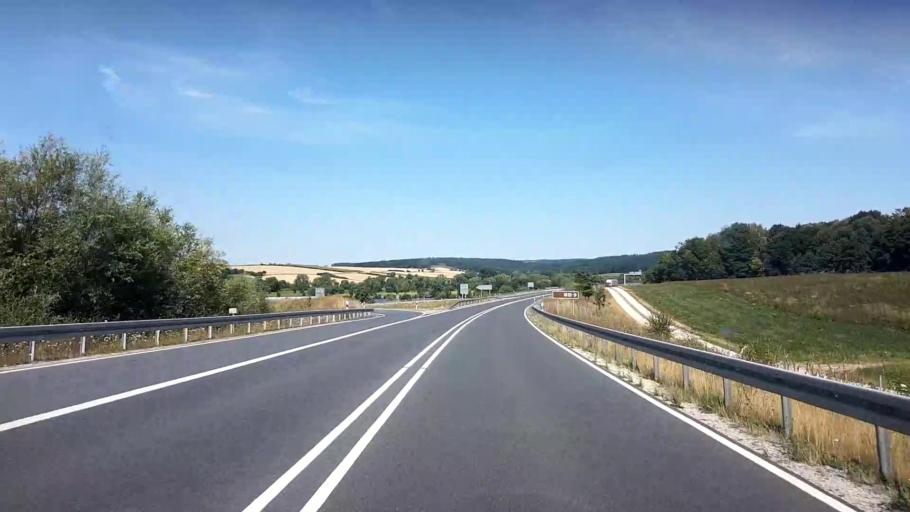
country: DE
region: Bavaria
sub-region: Upper Franconia
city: Grossheirath
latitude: 50.1841
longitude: 10.9605
